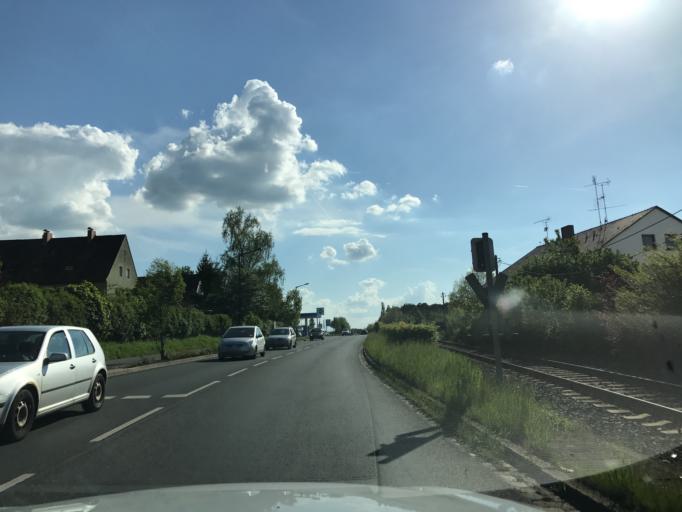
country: DE
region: Bavaria
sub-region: Upper Franconia
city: Igensdorf
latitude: 49.5902
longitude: 11.2185
